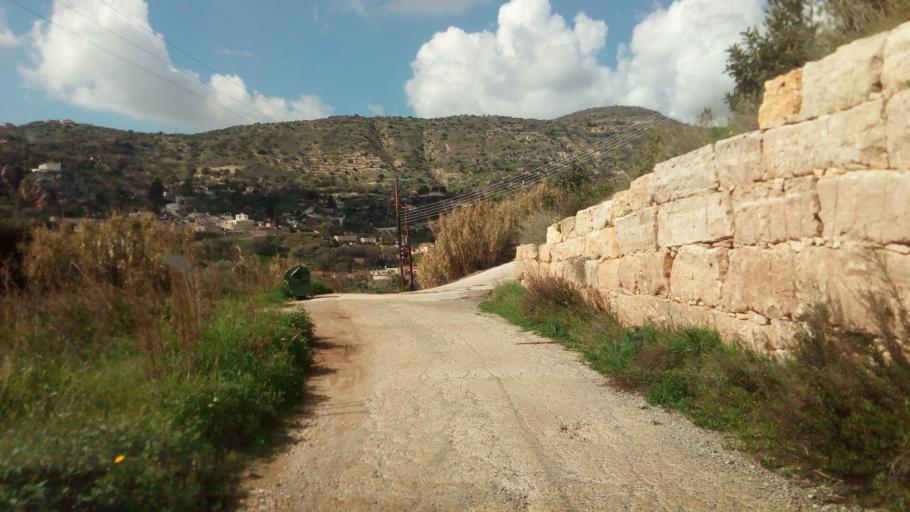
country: CY
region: Pafos
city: Mesogi
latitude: 34.7957
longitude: 32.5321
